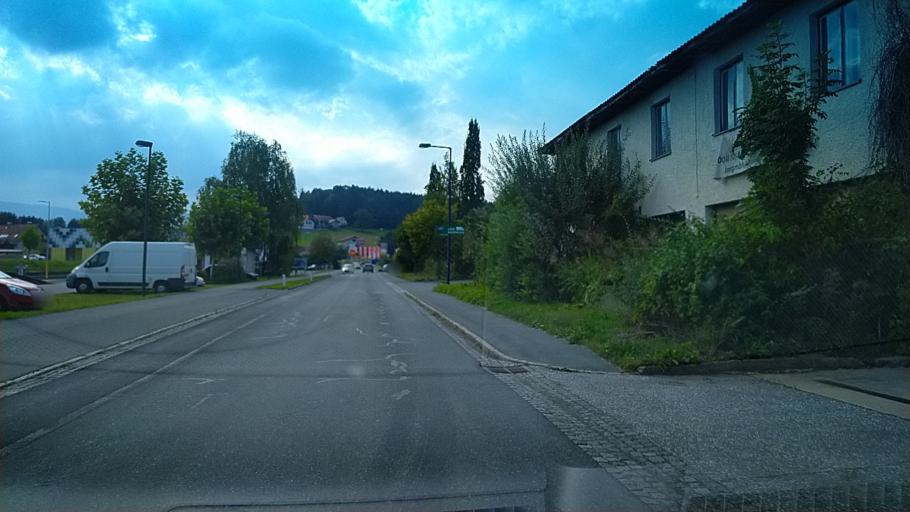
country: AT
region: Styria
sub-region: Politischer Bezirk Deutschlandsberg
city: Wies
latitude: 46.7188
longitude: 15.2582
